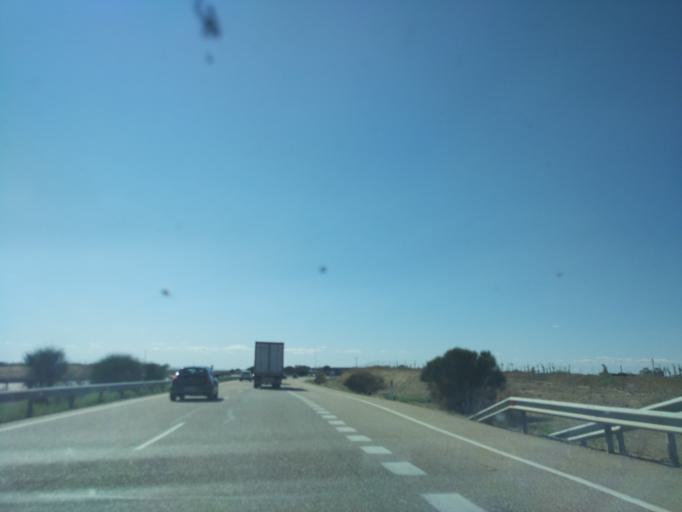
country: ES
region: Castille and Leon
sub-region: Provincia de Zamora
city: Villalpando
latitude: 41.8549
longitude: -5.4155
